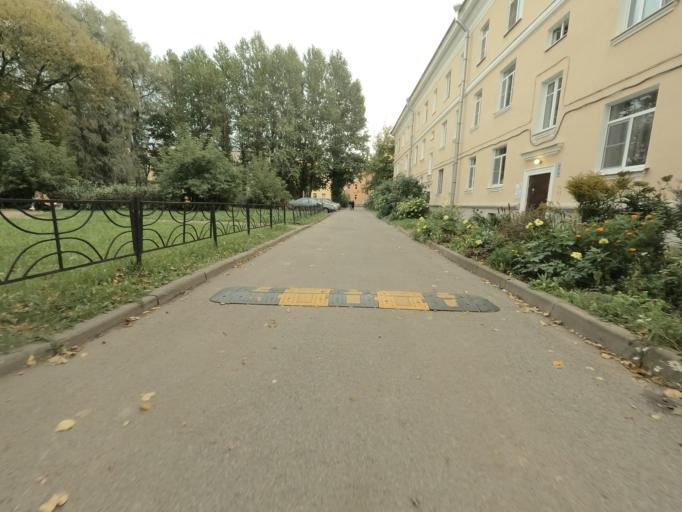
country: RU
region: St.-Petersburg
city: Pontonnyy
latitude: 59.7849
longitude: 30.6234
